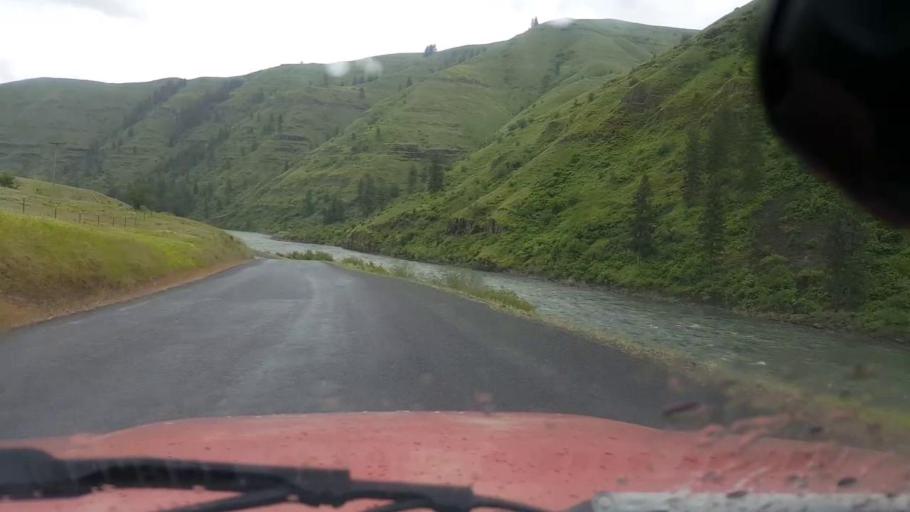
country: US
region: Washington
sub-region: Asotin County
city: Asotin
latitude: 46.0388
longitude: -117.2863
